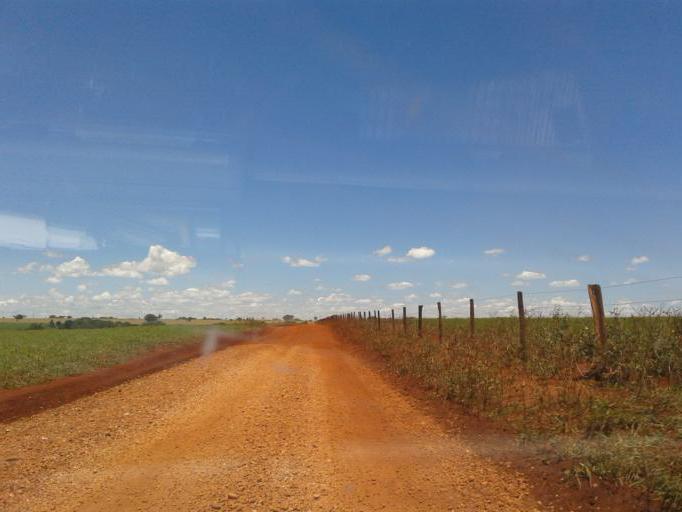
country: BR
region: Minas Gerais
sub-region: Capinopolis
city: Capinopolis
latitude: -18.5683
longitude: -49.5260
